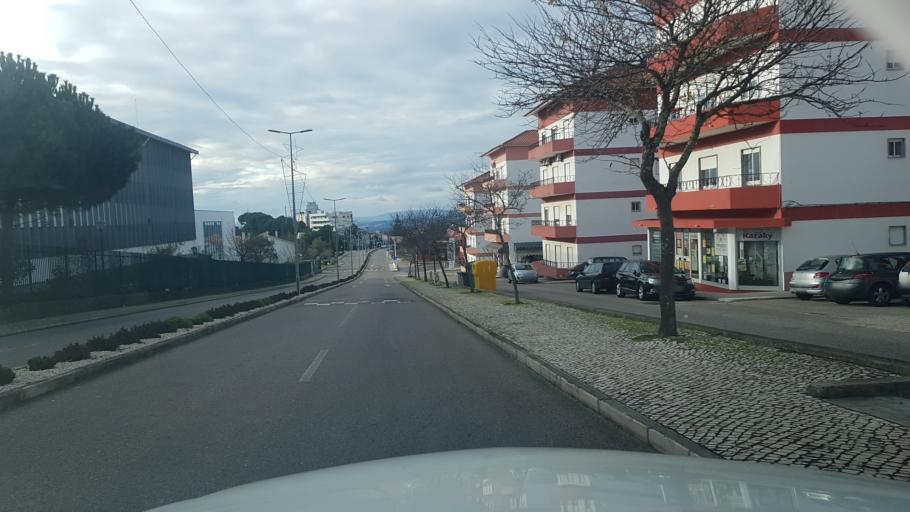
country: PT
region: Santarem
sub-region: Abrantes
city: Abrantes
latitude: 39.4630
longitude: -8.2077
